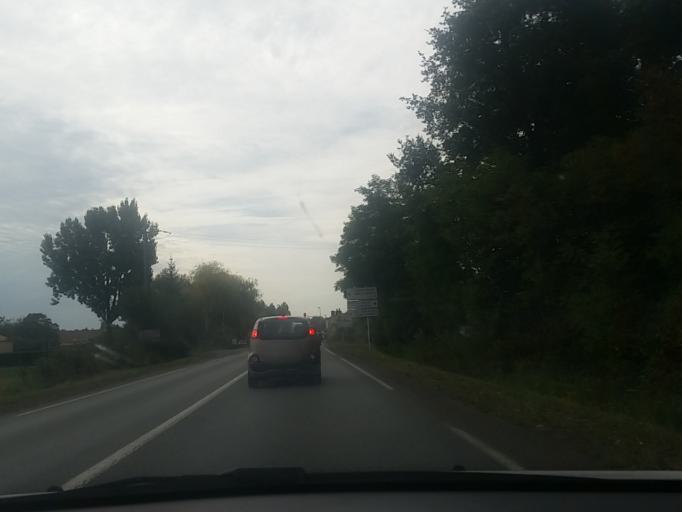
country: FR
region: Pays de la Loire
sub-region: Departement de la Vendee
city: Vendrennes
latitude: 46.8118
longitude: -1.1408
